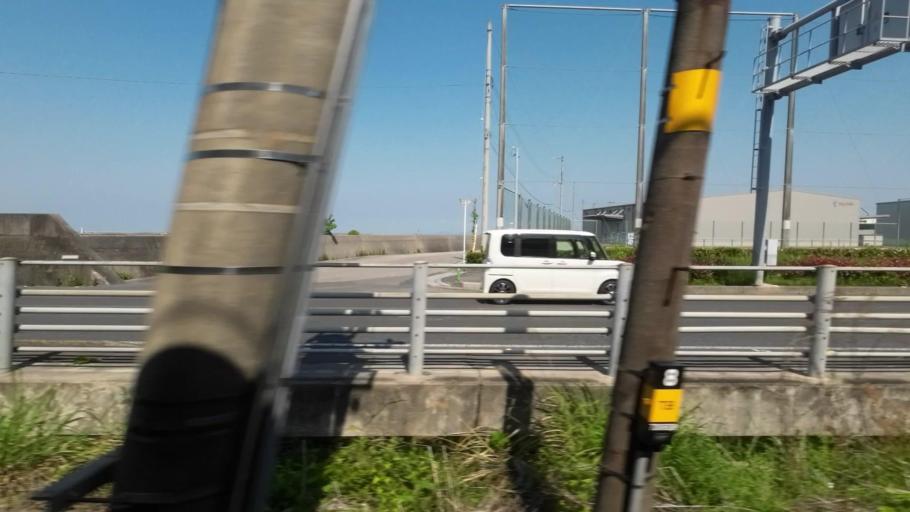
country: JP
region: Ehime
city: Kawanoecho
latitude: 34.0240
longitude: 133.5804
